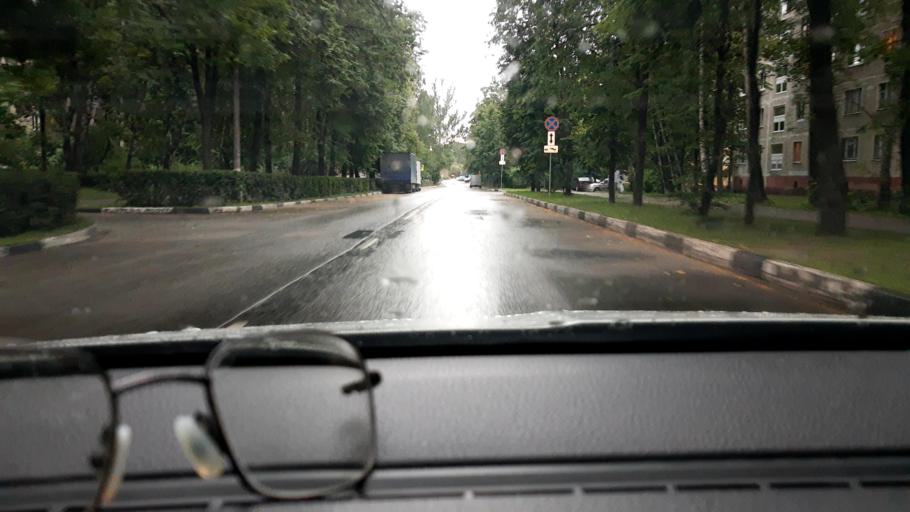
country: RU
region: Moskovskaya
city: Mytishchi
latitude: 55.9059
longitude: 37.7320
